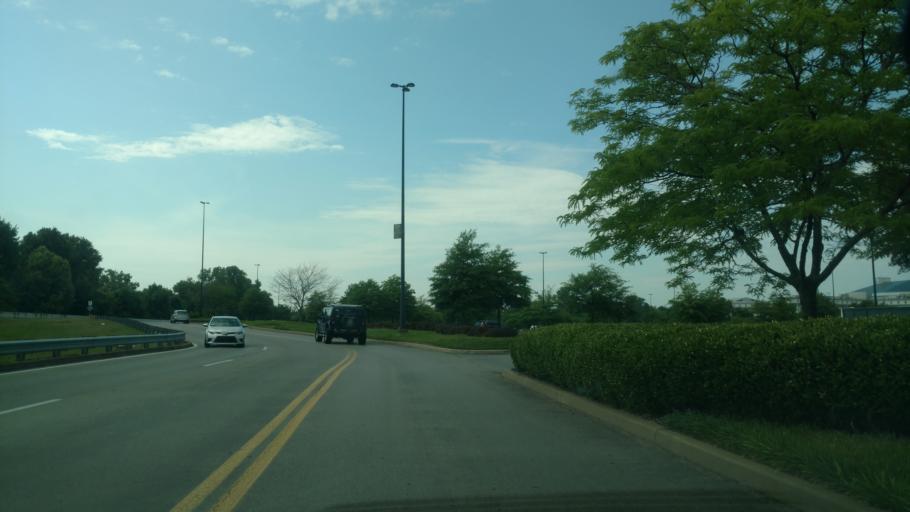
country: US
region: Tennessee
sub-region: Davidson County
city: Lakewood
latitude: 36.2061
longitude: -86.6967
